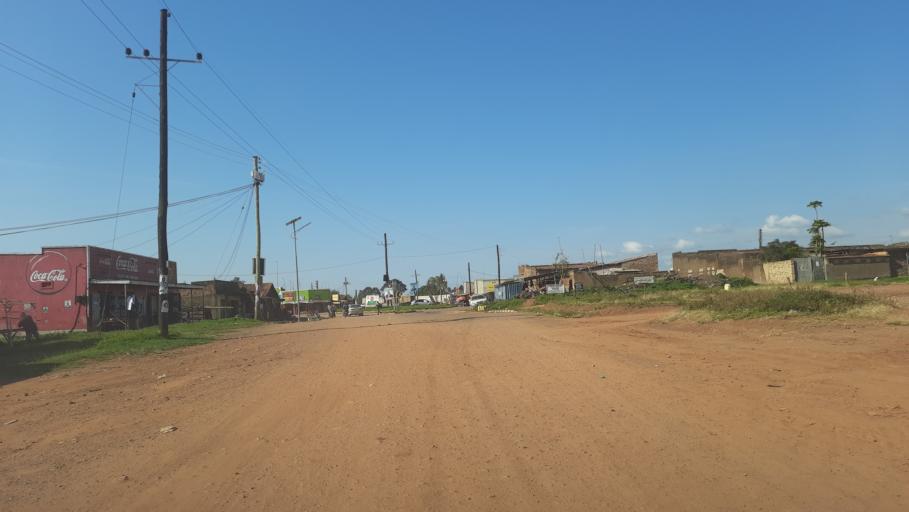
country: UG
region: Central Region
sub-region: Buikwe District
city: Buikwe
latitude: 0.2384
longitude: 32.9226
